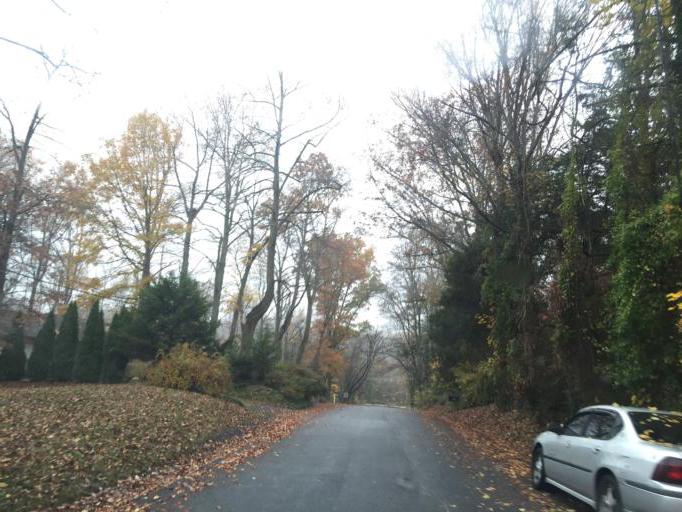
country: US
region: Maryland
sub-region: Howard County
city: Columbia
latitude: 39.2009
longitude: -76.8523
